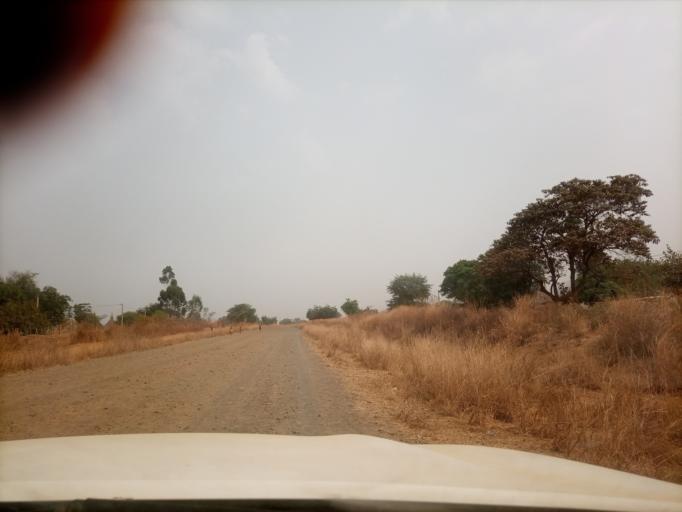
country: ET
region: Oromiya
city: Mendi
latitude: 10.1747
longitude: 35.0894
